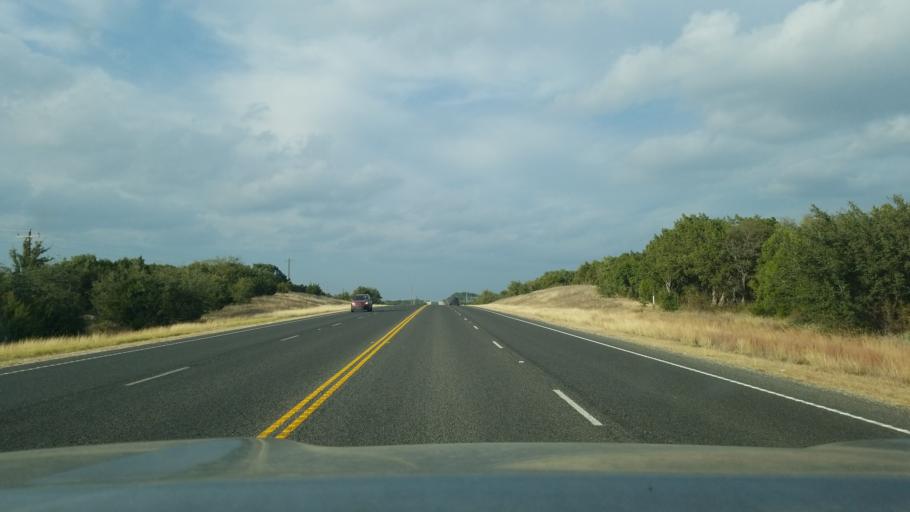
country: US
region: Texas
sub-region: Mills County
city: Goldthwaite
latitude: 31.4203
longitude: -98.5657
